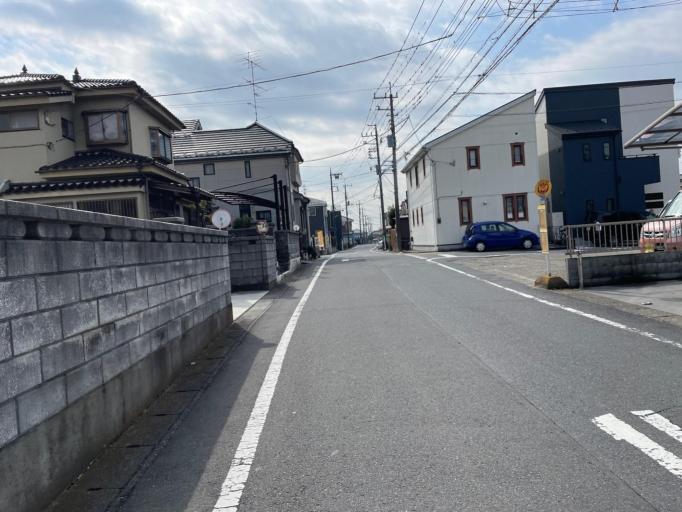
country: JP
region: Saitama
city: Yoshikawa
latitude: 35.8660
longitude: 139.8408
